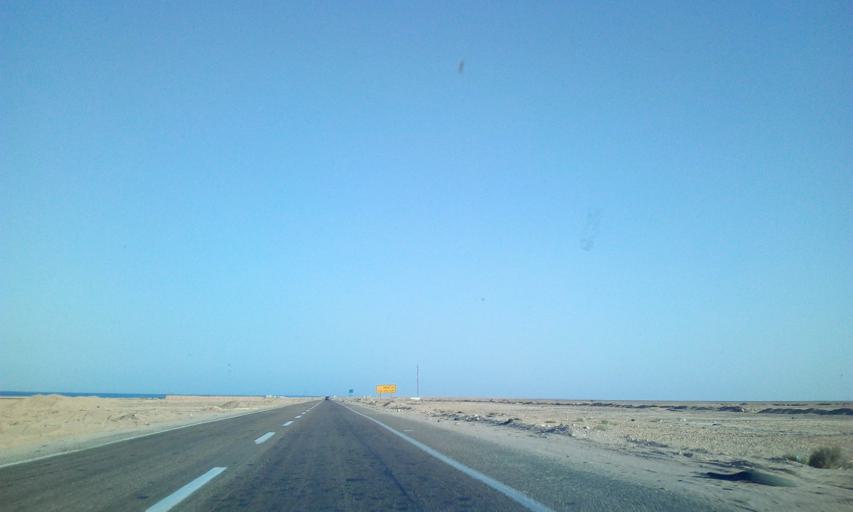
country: EG
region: South Sinai
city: Tor
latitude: 28.5337
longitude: 32.9290
